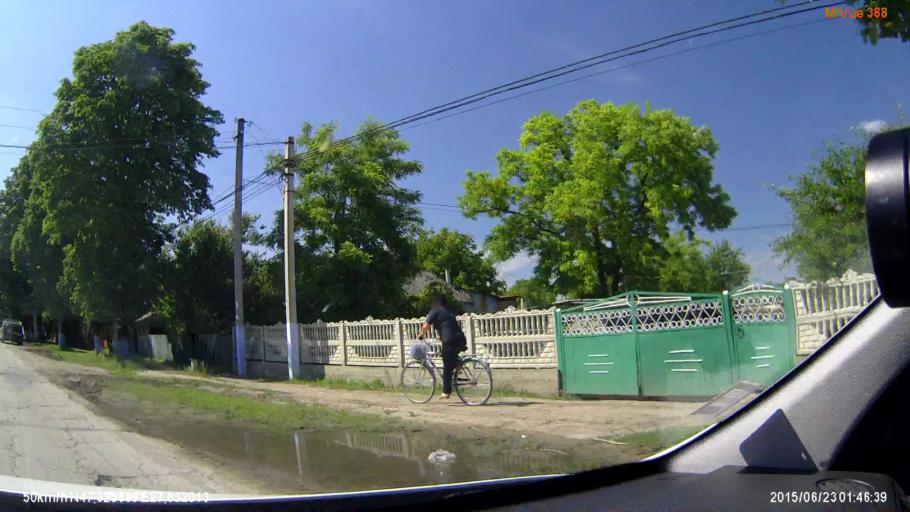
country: RO
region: Iasi
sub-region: Comuna Victoria
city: Victoria
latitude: 47.3258
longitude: 27.6322
